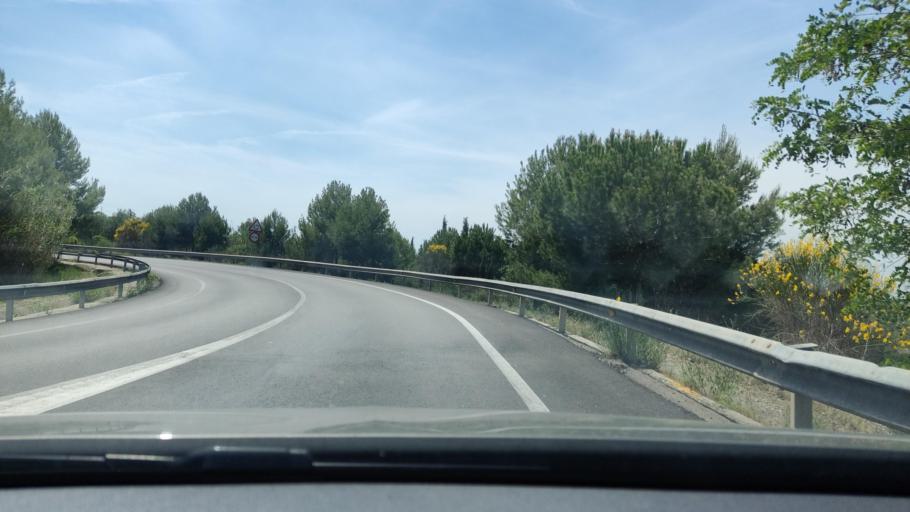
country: ES
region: Catalonia
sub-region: Provincia de Barcelona
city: Sant Sadurni d'Anoia
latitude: 41.4186
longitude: 1.7923
